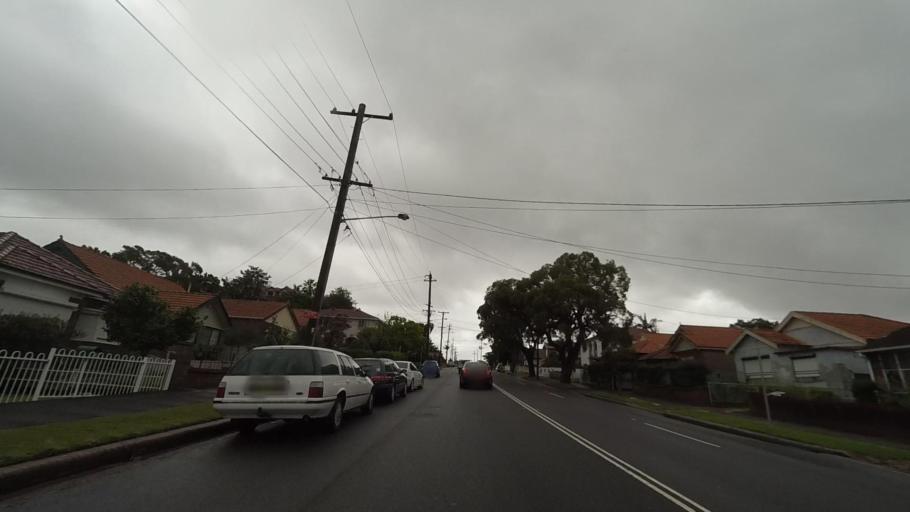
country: AU
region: New South Wales
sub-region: Kogarah
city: Kogarah Bay
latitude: -33.9777
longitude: 151.1217
